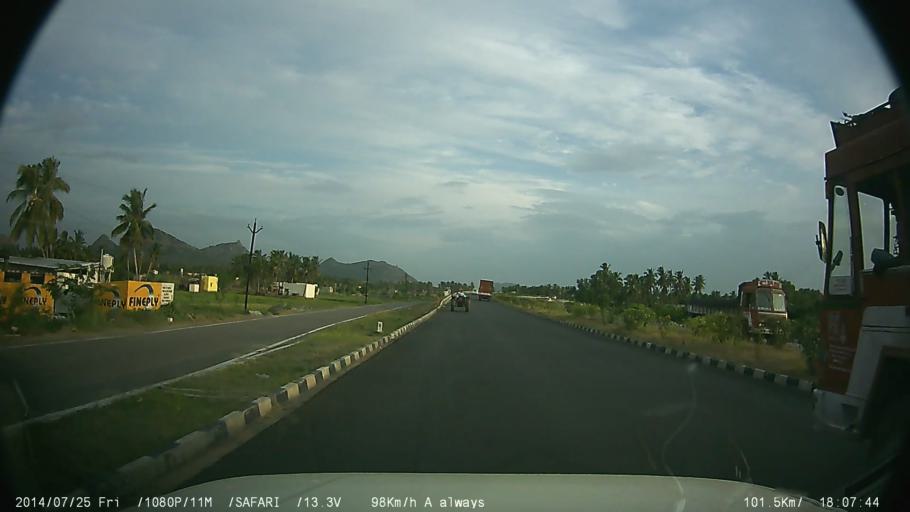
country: IN
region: Tamil Nadu
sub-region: Krishnagiri
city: Kaverippattanam
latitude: 12.4096
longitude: 78.2239
